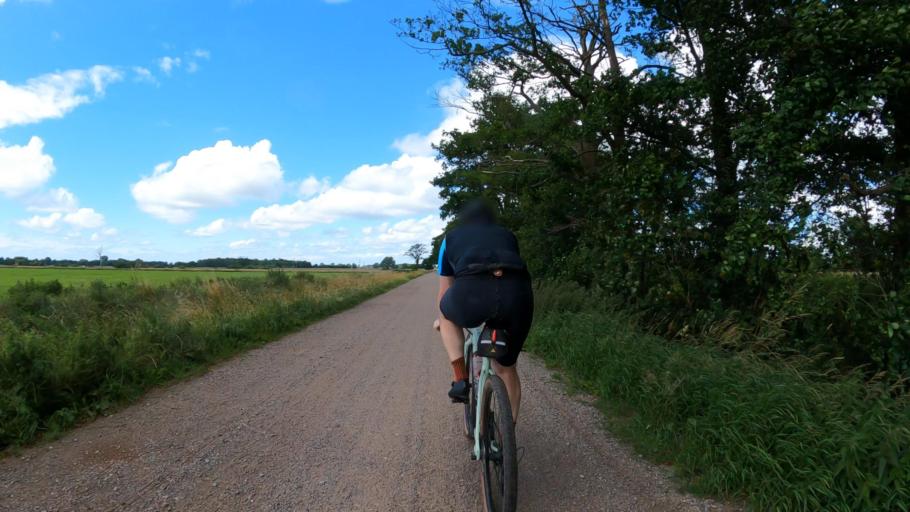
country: DE
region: Lower Saxony
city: Neu Wulmstorf
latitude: 53.4673
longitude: 9.7581
